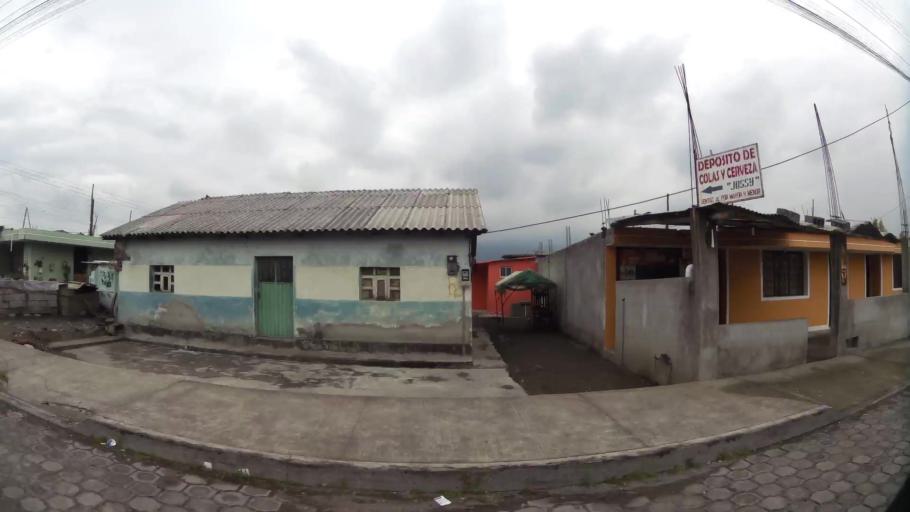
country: EC
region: Pichincha
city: Sangolqui
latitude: -0.3375
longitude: -78.4652
